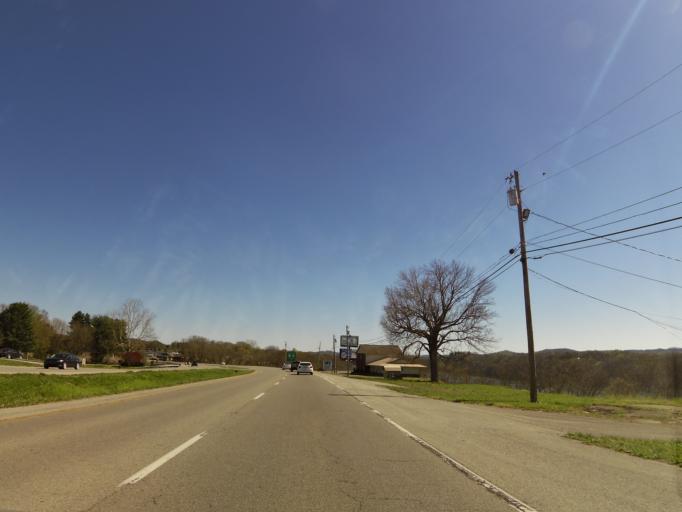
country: US
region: Kentucky
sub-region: Pulaski County
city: Somerset
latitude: 37.0120
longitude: -84.6267
